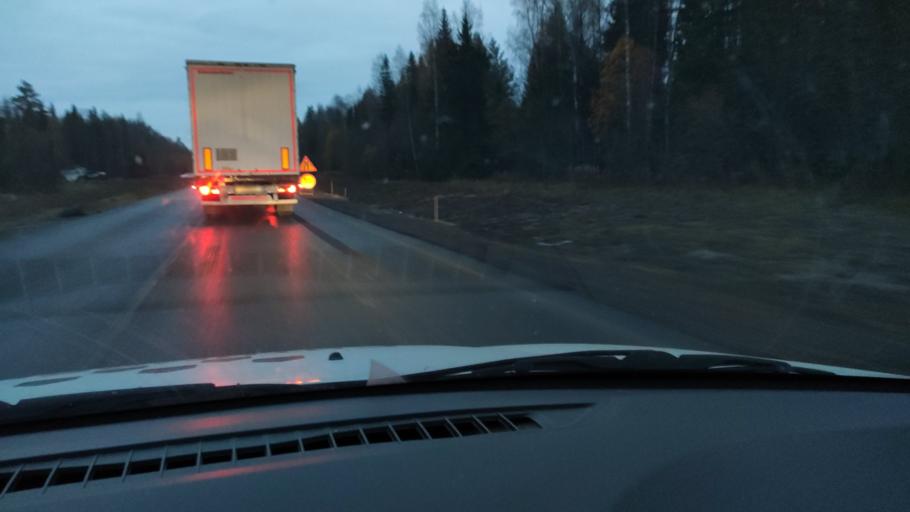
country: RU
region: Kirov
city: Kostino
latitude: 58.8215
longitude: 53.3559
